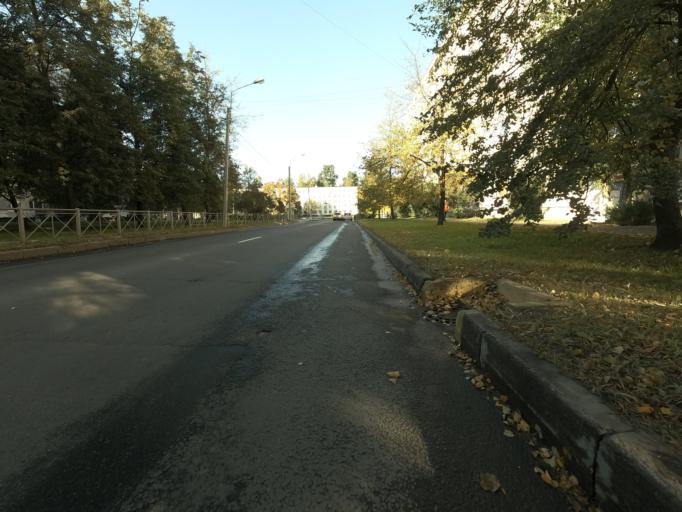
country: RU
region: St.-Petersburg
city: Kolpino
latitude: 59.7408
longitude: 30.5692
